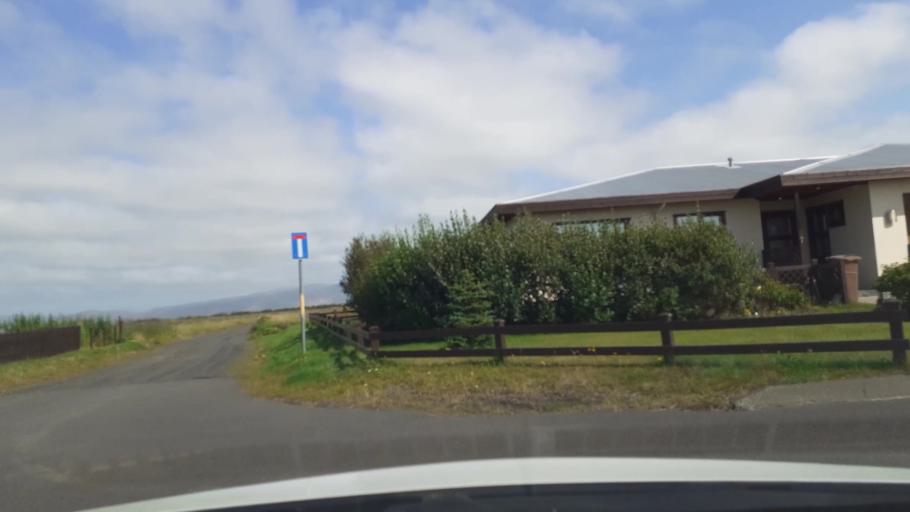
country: IS
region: South
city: Hveragerdi
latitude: 63.8641
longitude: -21.1472
